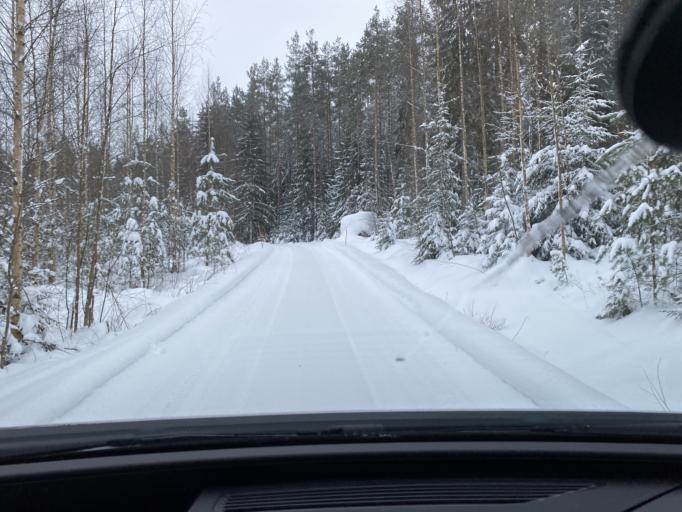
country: FI
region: Pirkanmaa
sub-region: Lounais-Pirkanmaa
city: Punkalaidun
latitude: 61.1352
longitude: 23.0939
